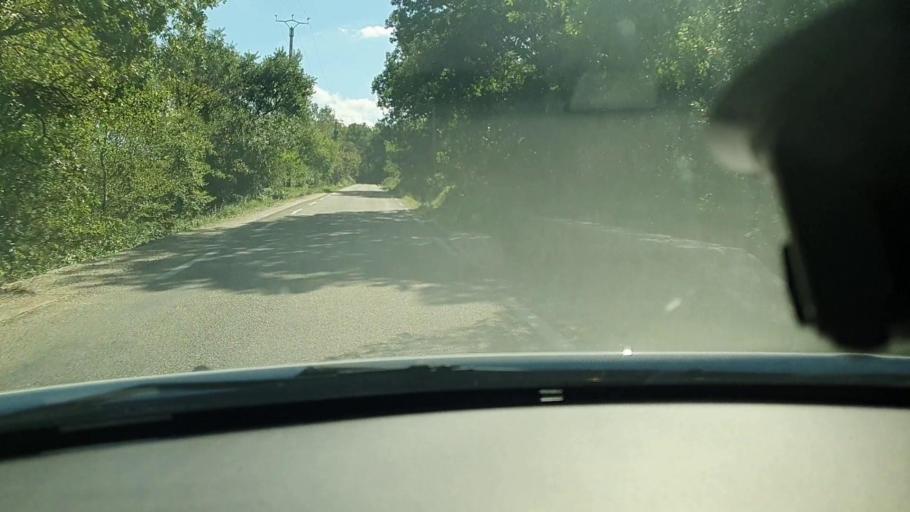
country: FR
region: Languedoc-Roussillon
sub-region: Departement du Gard
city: Goudargues
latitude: 44.1802
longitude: 4.4776
